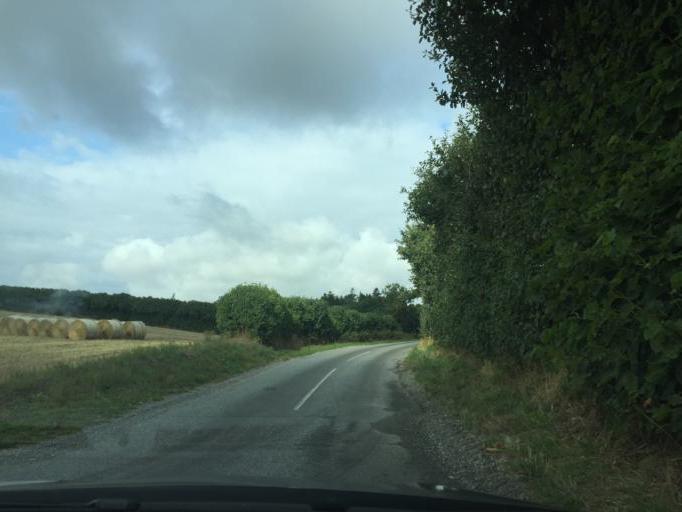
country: DK
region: South Denmark
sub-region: Assens Kommune
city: Harby
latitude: 55.1944
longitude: 10.1987
